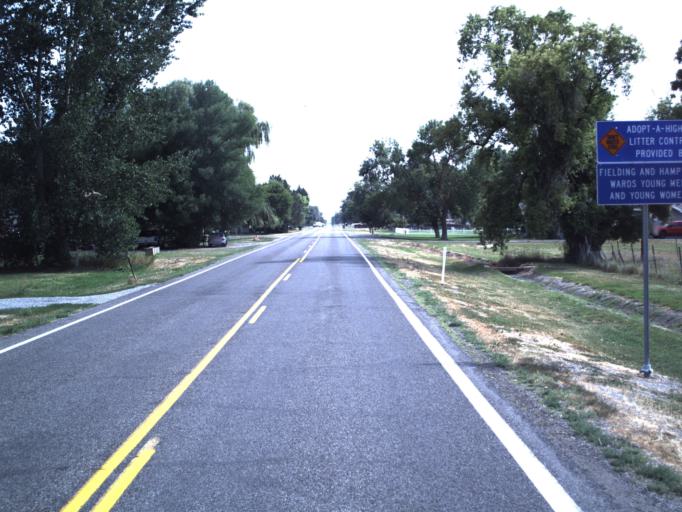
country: US
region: Utah
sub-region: Box Elder County
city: Garland
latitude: 41.8125
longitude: -112.1161
